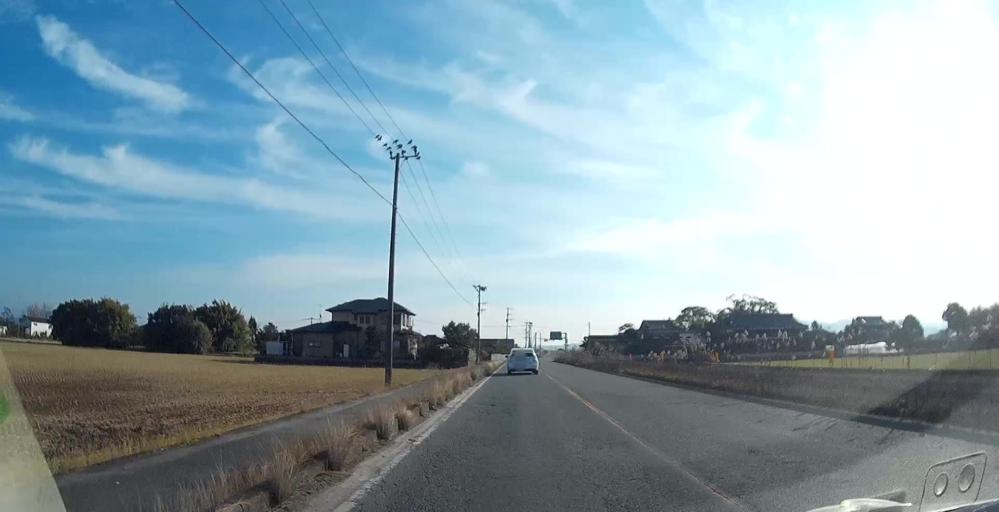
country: JP
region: Kumamoto
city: Uto
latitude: 32.7298
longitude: 130.6396
